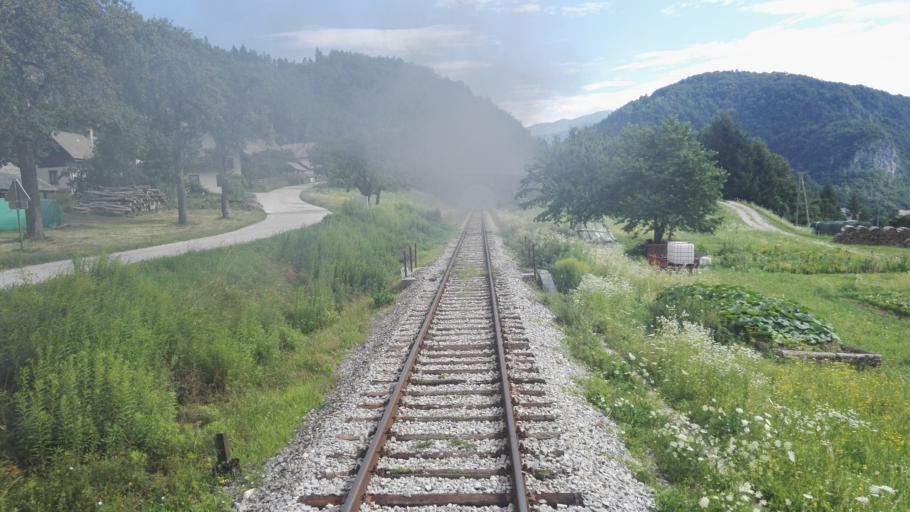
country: SI
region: Gorje
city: Zgornje Gorje
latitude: 46.3450
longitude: 14.0609
